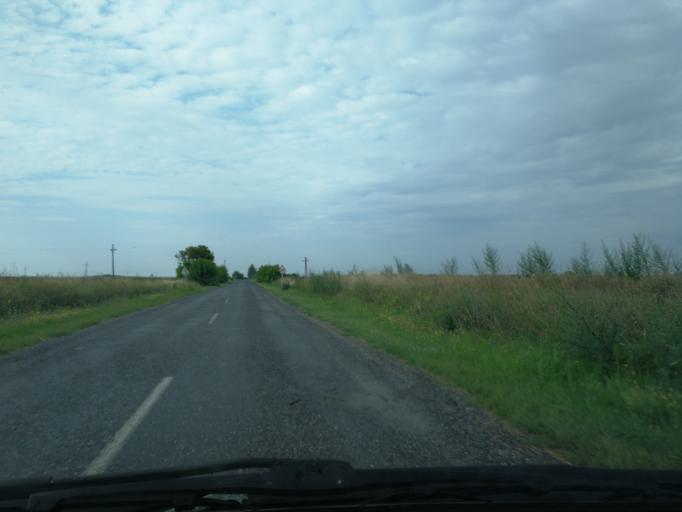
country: HU
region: Bacs-Kiskun
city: Kalocsa
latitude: 46.4840
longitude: 19.0510
